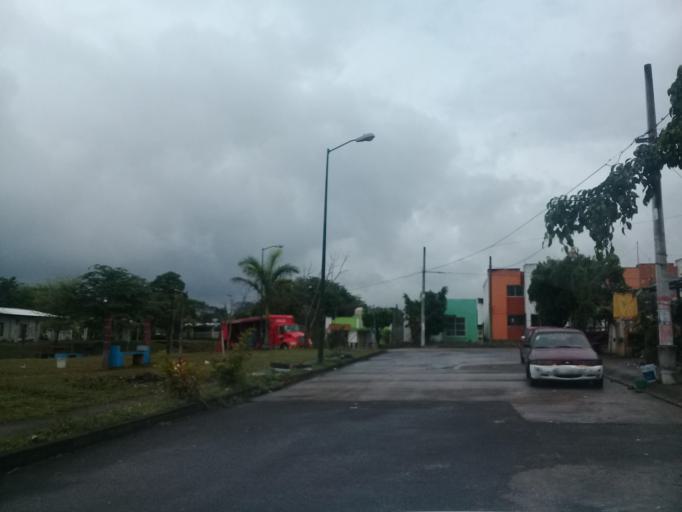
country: MX
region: Veracruz
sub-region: Cordoba
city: San Jose de Tapia
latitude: 18.8393
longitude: -96.9542
